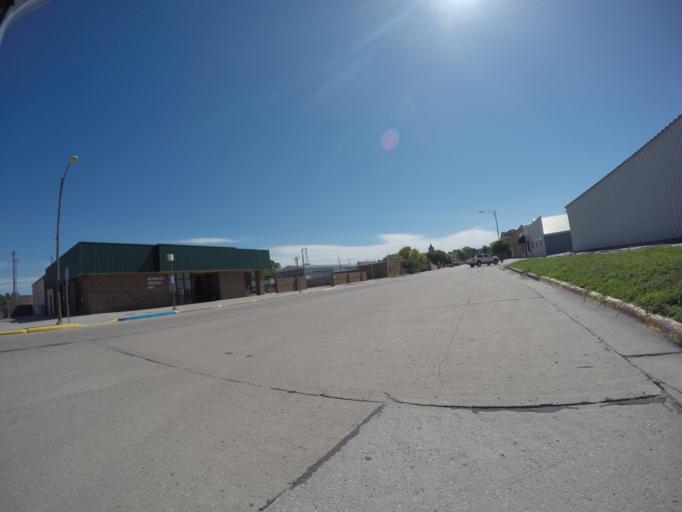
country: US
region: Kansas
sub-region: Rawlins County
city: Atwood
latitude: 39.8075
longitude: -101.0432
